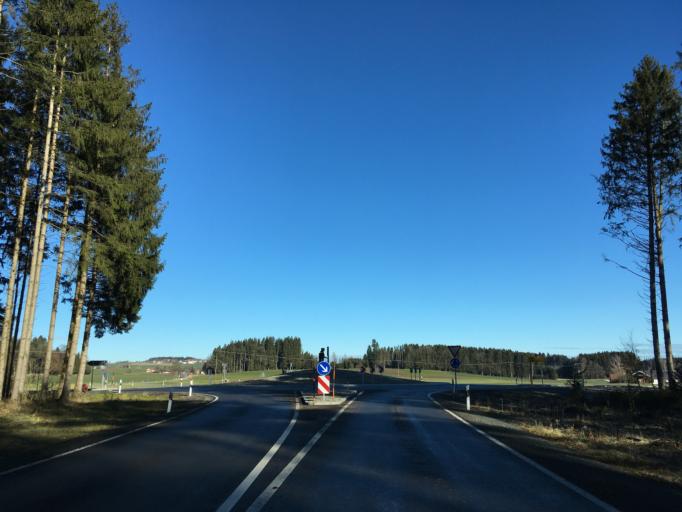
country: DE
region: Bavaria
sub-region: Upper Bavaria
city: Hoslwang
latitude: 47.9606
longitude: 12.3537
